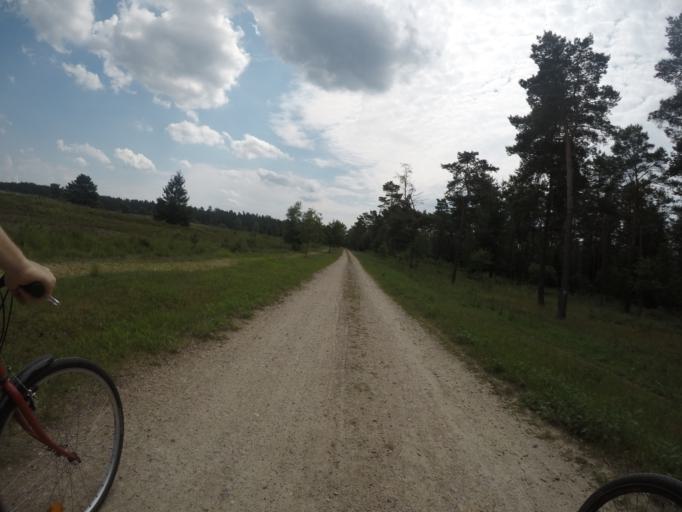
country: DE
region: Lower Saxony
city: Asendorf
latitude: 53.2484
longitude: 9.9563
